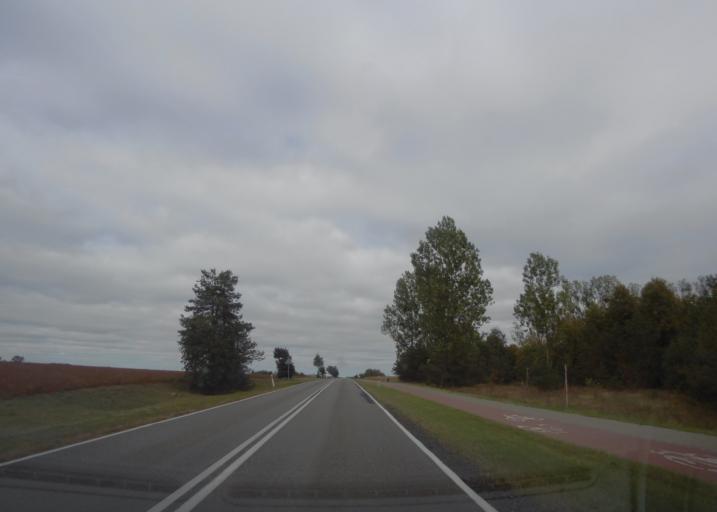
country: PL
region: Lublin Voivodeship
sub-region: Powiat wlodawski
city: Wlodawa
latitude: 51.5275
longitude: 23.5232
